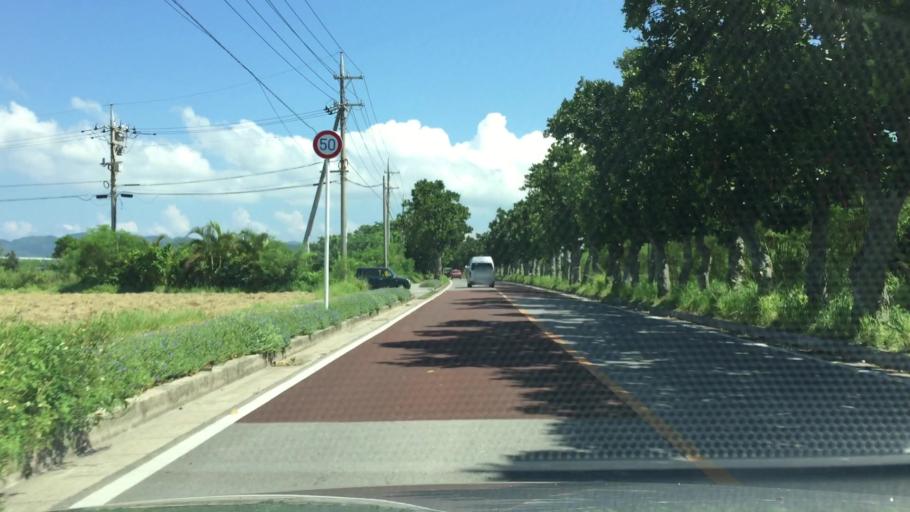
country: JP
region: Okinawa
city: Ishigaki
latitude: 24.3677
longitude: 124.2465
